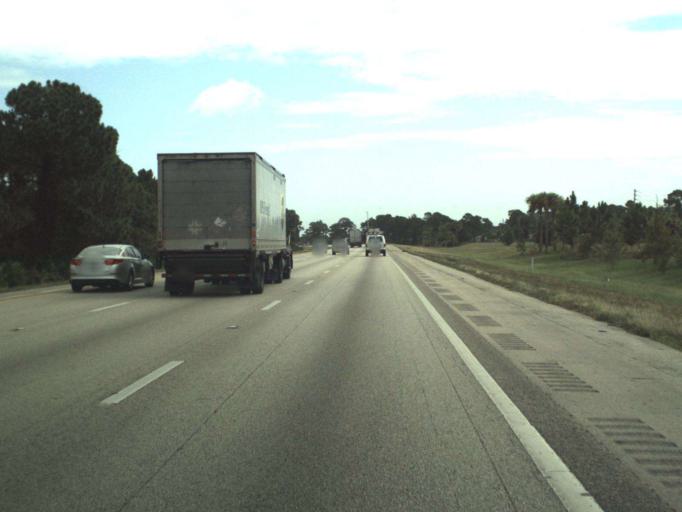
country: US
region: Florida
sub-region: Saint Lucie County
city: Port Saint Lucie
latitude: 27.2186
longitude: -80.4002
